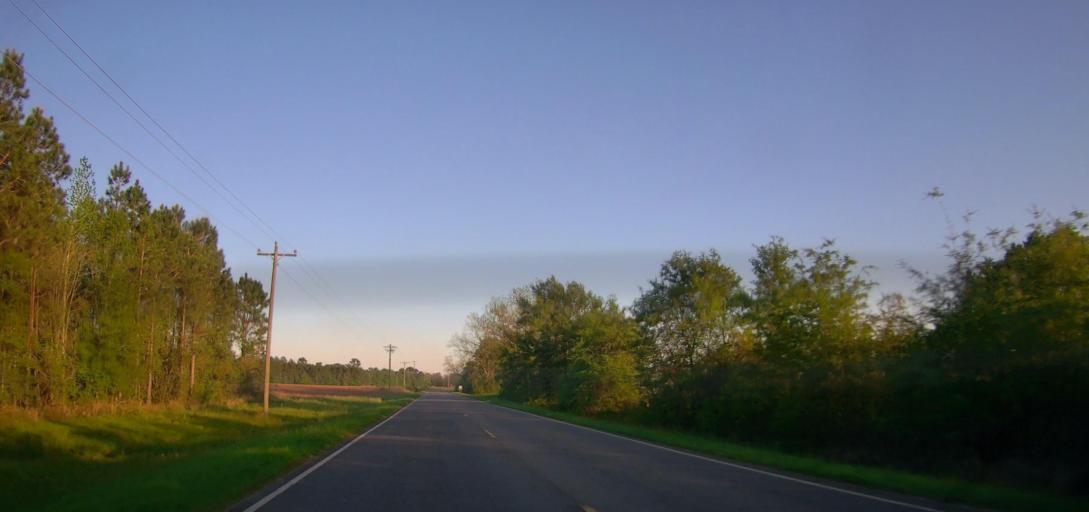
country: US
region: Georgia
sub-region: Irwin County
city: Ocilla
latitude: 31.6105
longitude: -83.2615
